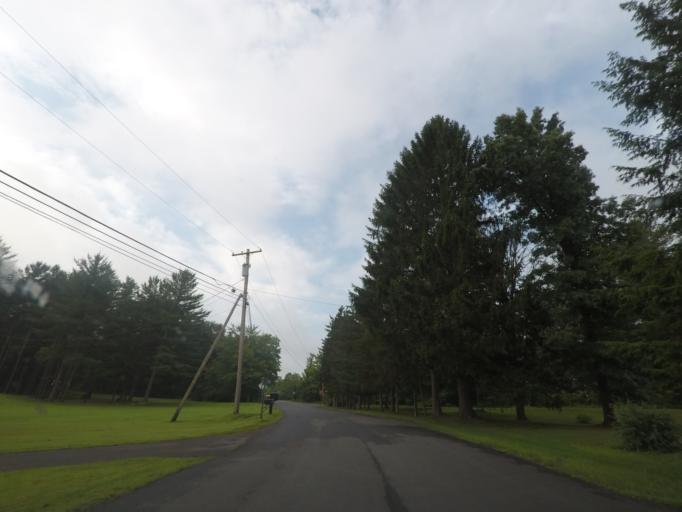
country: US
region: New York
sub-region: Rensselaer County
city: Nassau
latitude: 42.5446
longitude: -73.6083
